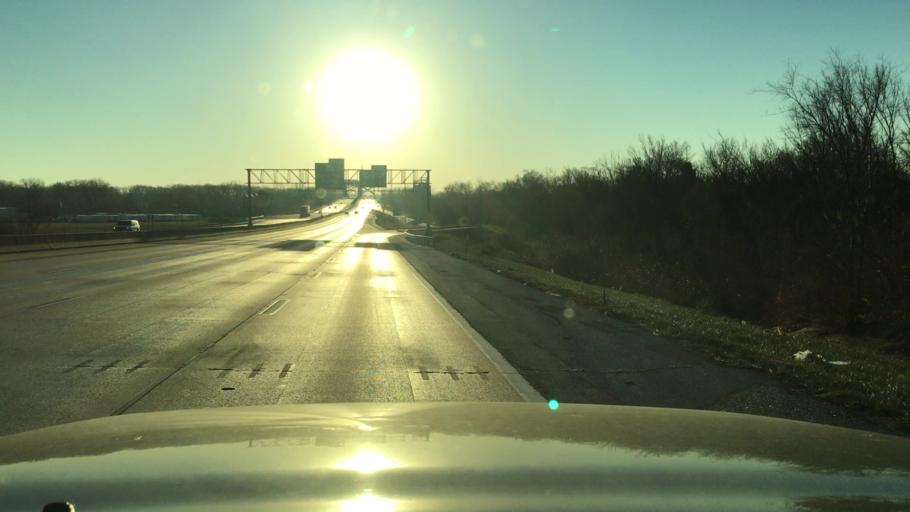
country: US
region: Missouri
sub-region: Saint Charles County
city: Saint Charles
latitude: 38.8052
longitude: -90.4791
